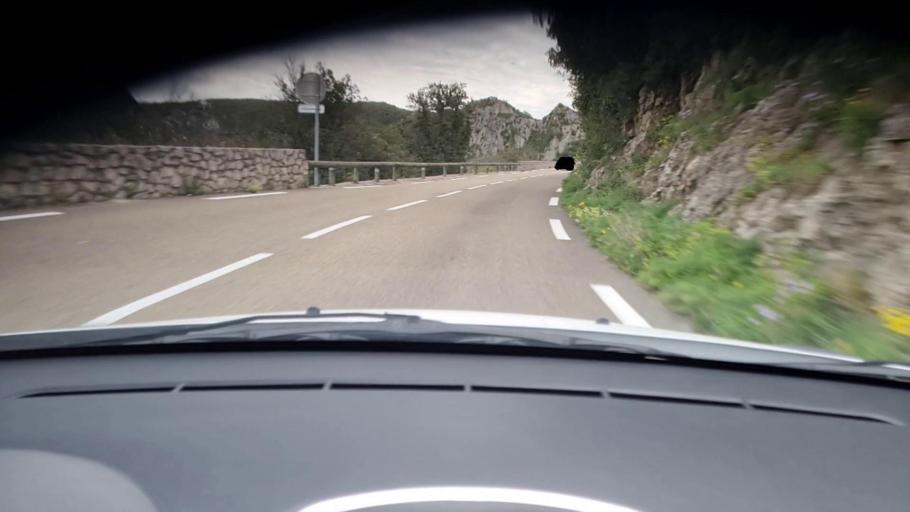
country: FR
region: Languedoc-Roussillon
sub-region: Departement du Gard
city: Blauzac
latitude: 43.9365
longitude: 4.3851
